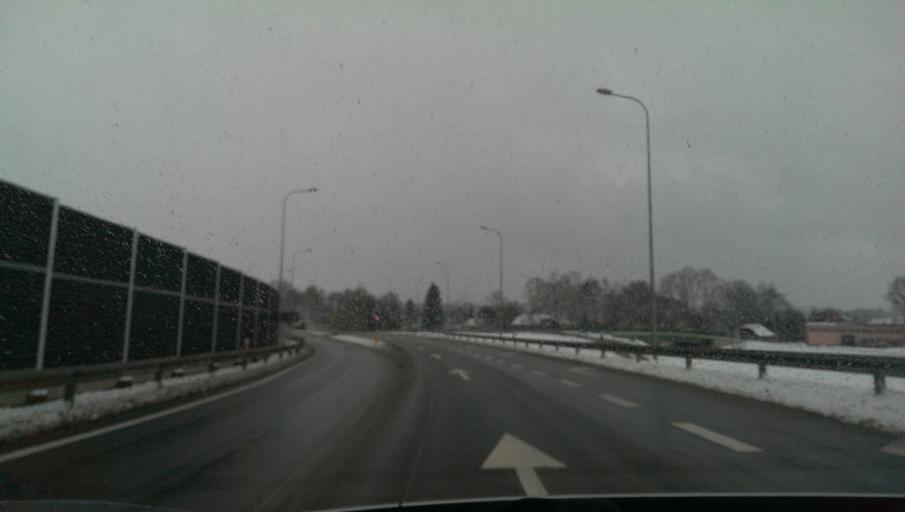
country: PL
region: Subcarpathian Voivodeship
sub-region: Powiat brzozowski
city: Brzozow
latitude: 49.6932
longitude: 22.0304
